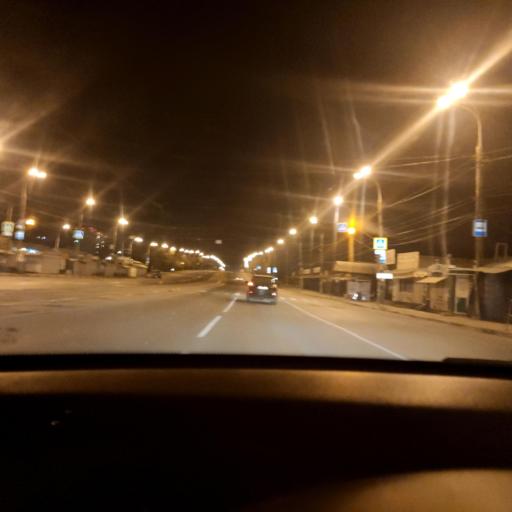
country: RU
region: Samara
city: Smyshlyayevka
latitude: 53.2093
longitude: 50.2751
